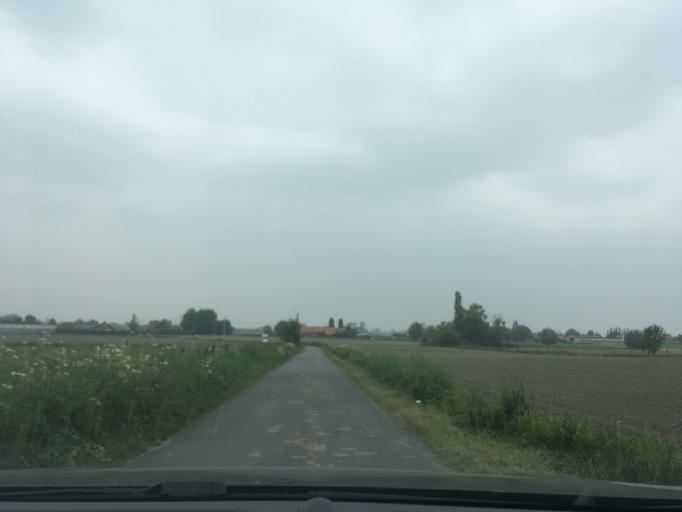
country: BE
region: Flanders
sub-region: Provincie West-Vlaanderen
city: Hooglede
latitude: 50.9991
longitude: 3.1231
